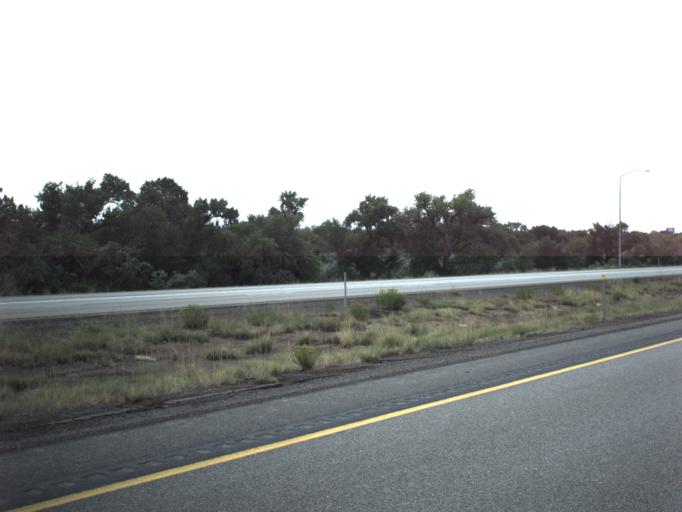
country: US
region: Utah
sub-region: Carbon County
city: Carbonville
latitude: 39.6059
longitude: -110.8317
